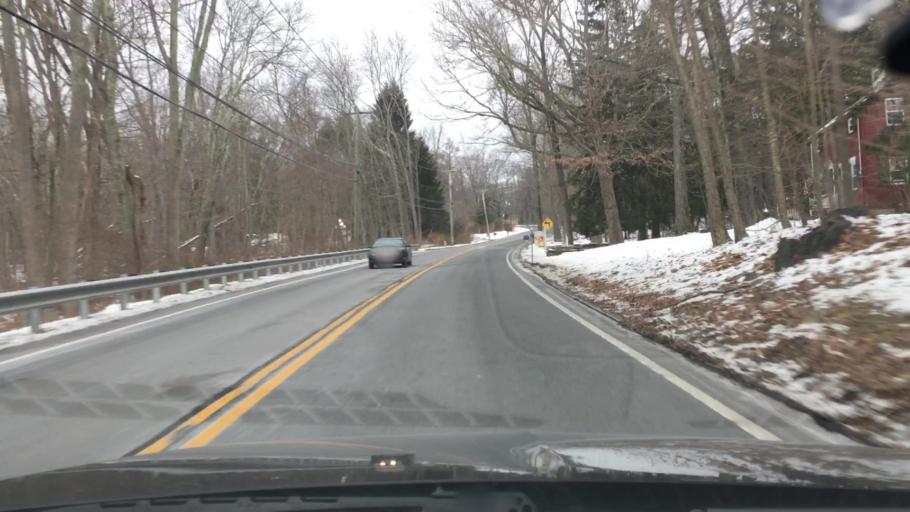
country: US
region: Connecticut
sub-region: Tolland County
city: Tolland
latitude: 41.8478
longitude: -72.3270
